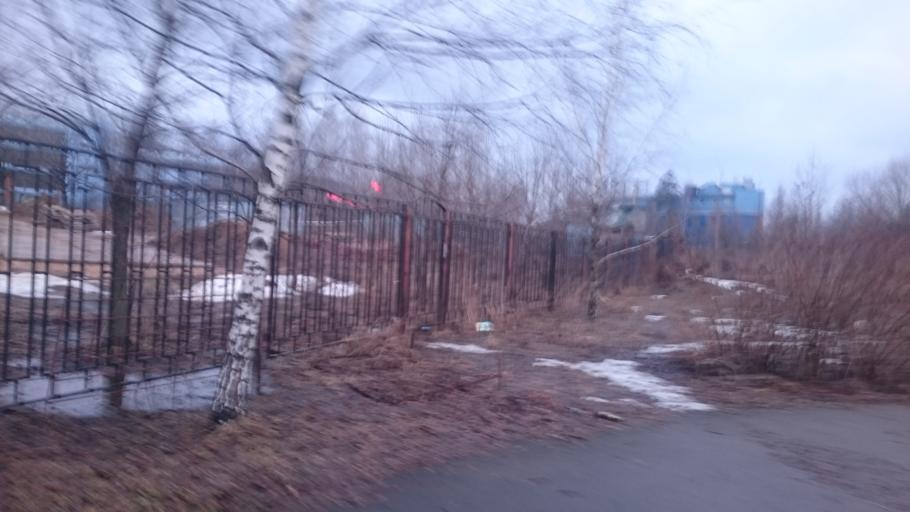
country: RU
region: Moskovskaya
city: Novoivanovskoye
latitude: 55.7028
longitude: 37.3590
